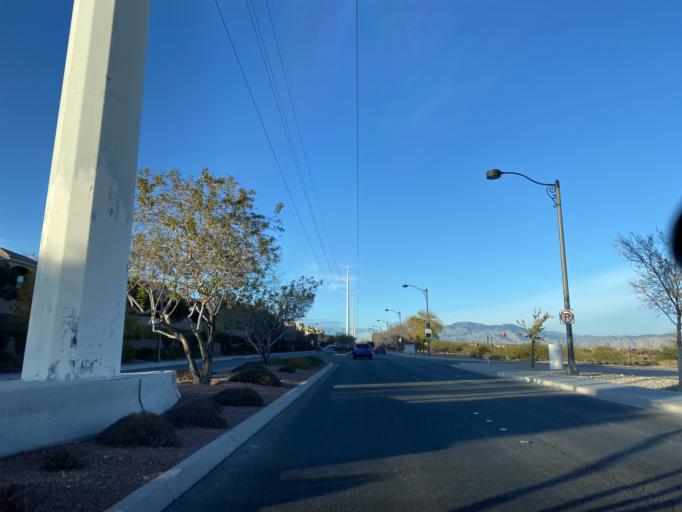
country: US
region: Nevada
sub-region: Clark County
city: Summerlin South
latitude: 36.2844
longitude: -115.3288
